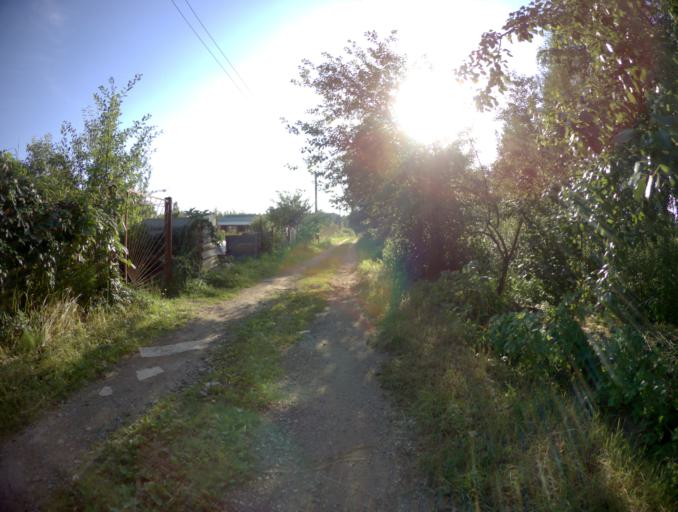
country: RU
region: Vladimir
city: Bogolyubovo
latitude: 56.1027
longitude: 40.5573
